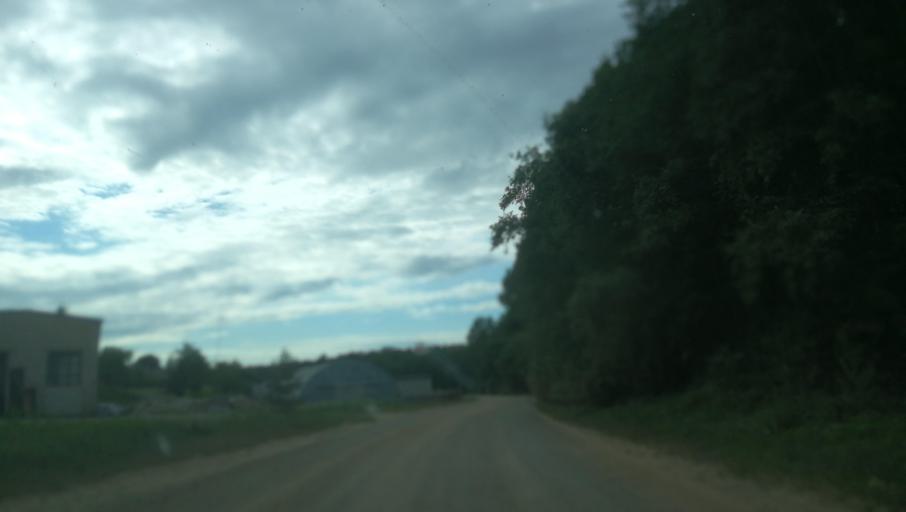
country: LV
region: Cesu Rajons
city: Cesis
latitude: 57.3219
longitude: 25.2691
